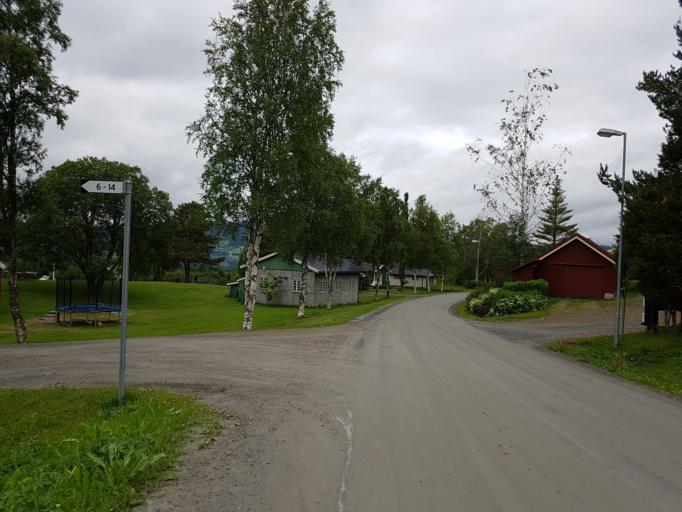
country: NO
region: Sor-Trondelag
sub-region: Selbu
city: Mebonden
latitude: 63.2256
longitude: 11.0301
